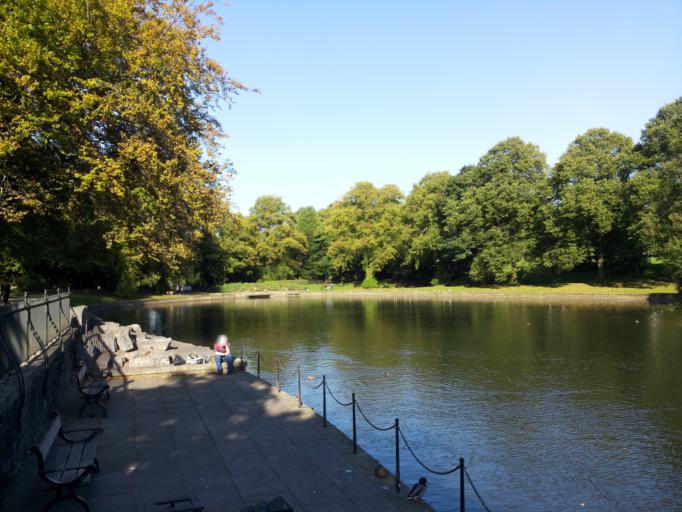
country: GB
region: England
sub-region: Derbyshire
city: Buxton
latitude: 53.2552
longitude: -1.9194
